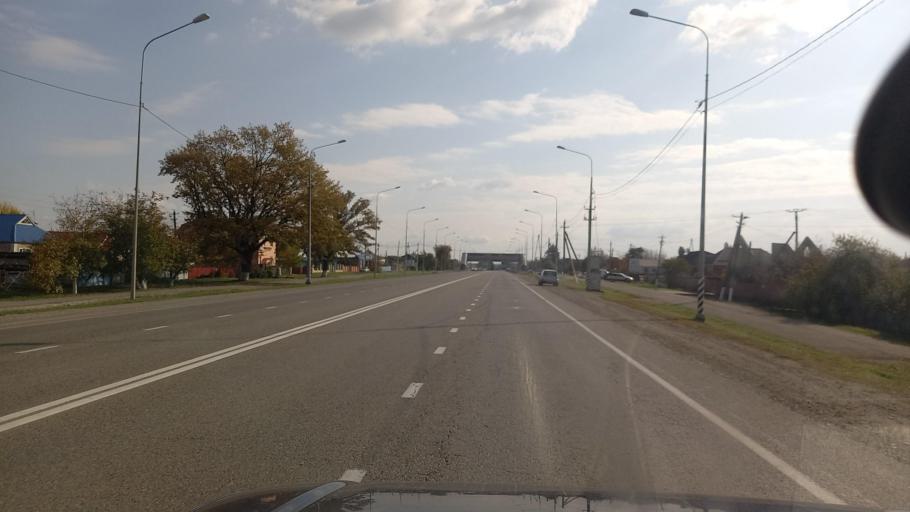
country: RU
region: Krasnodarskiy
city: Novoukrainskiy
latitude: 44.8973
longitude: 38.0461
